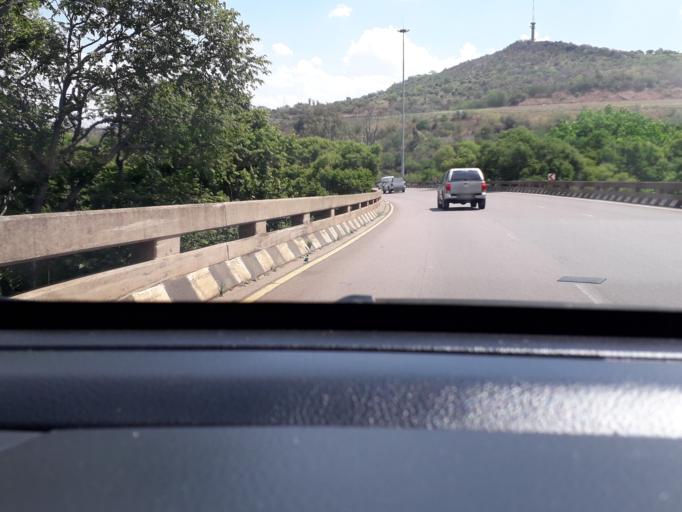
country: ZA
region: Gauteng
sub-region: City of Tshwane Metropolitan Municipality
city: Pretoria
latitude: -25.7745
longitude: 28.1958
